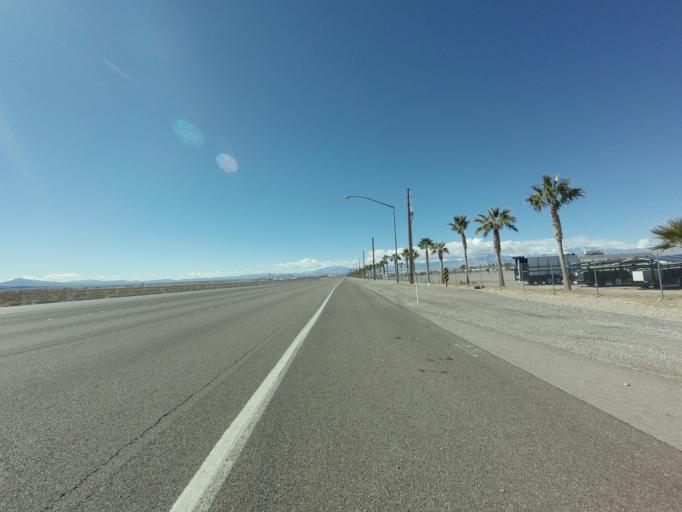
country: US
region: Nevada
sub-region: Clark County
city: Nellis Air Force Base
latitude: 36.2635
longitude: -115.0152
